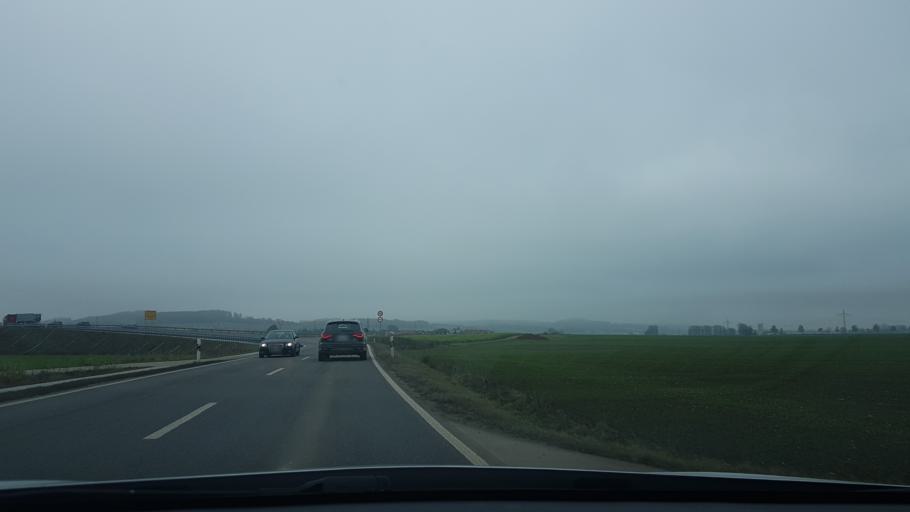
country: DE
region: Bavaria
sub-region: Lower Bavaria
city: Essenbach
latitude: 48.6146
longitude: 12.2314
